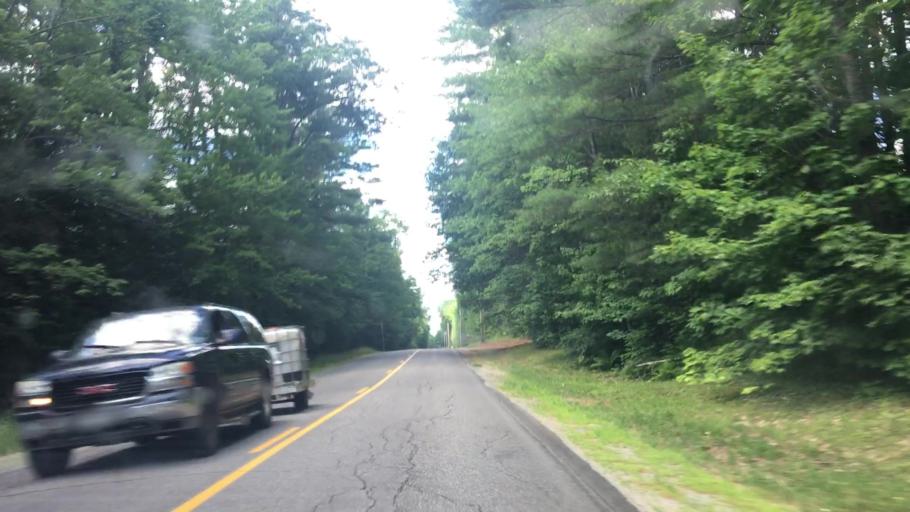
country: US
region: Maine
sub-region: Franklin County
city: Chesterville
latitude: 44.5999
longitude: -70.0846
